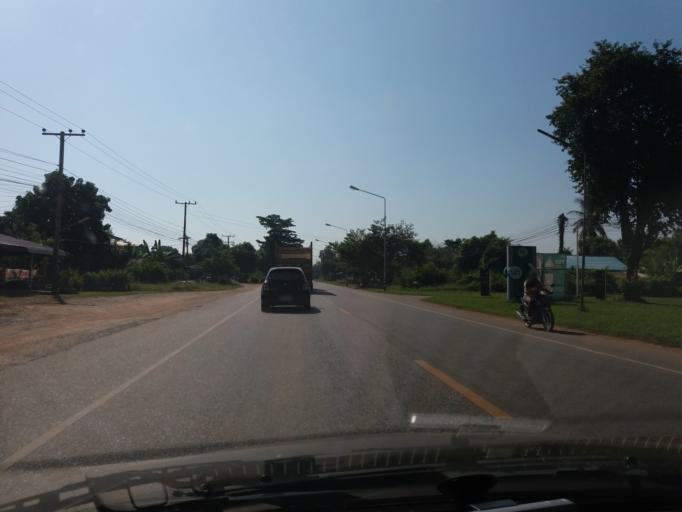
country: TH
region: Kamphaeng Phet
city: Khlong Khlung
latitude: 16.1676
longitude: 99.8005
